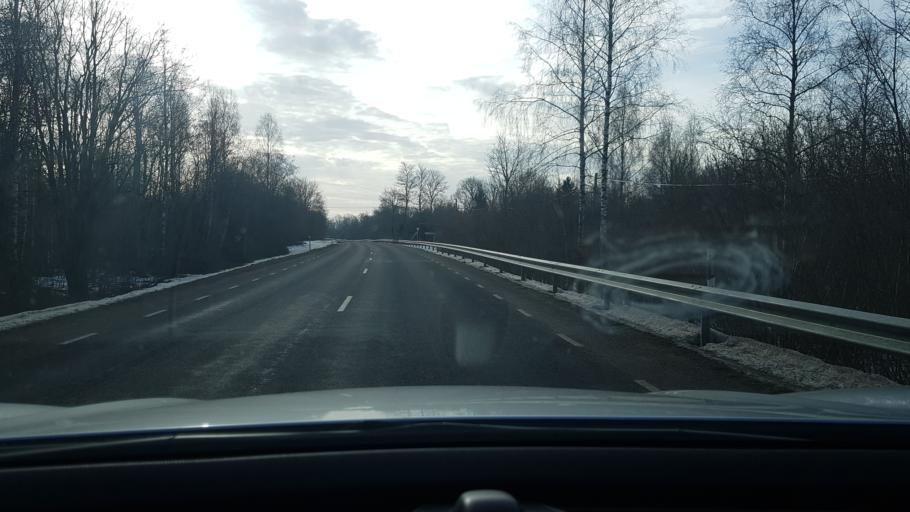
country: EE
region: Saare
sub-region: Kuressaare linn
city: Kuressaare
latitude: 58.3040
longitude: 22.5393
